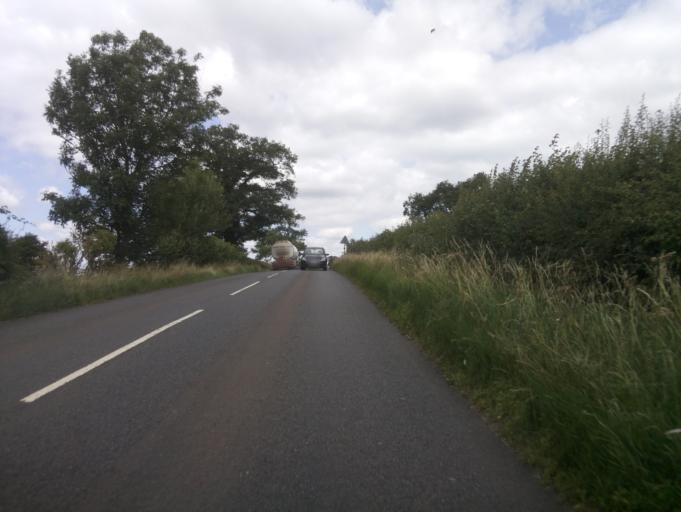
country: GB
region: England
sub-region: Buckinghamshire
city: Newton Longville
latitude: 51.9750
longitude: -0.8219
